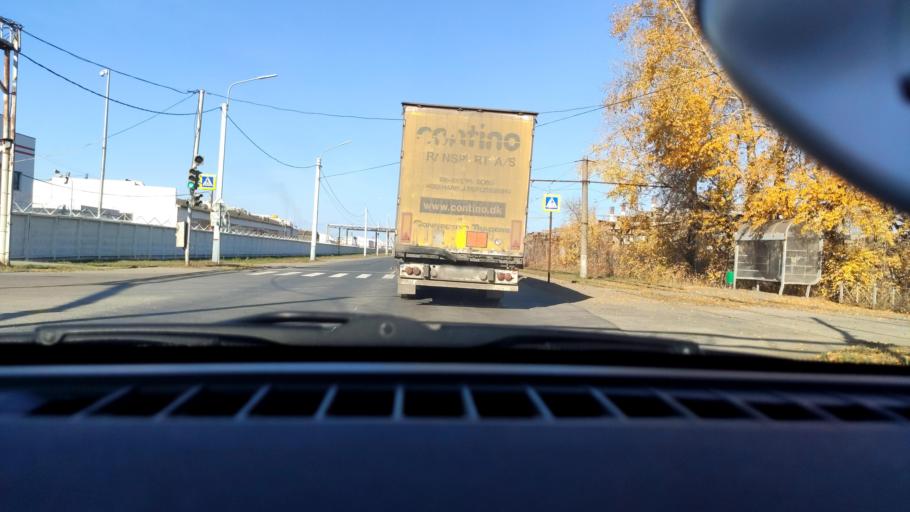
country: RU
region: Perm
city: Gamovo
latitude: 57.9141
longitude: 56.1553
